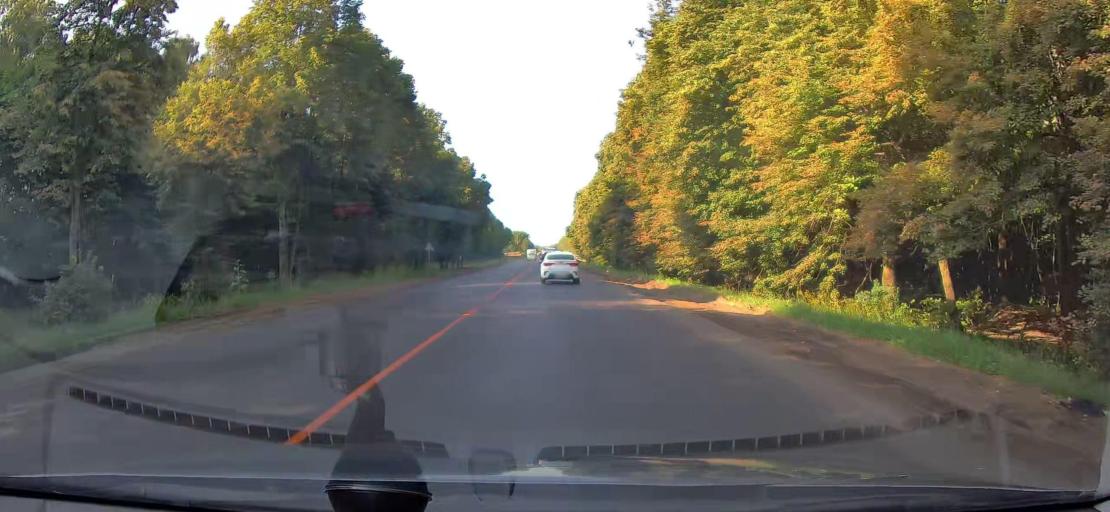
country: RU
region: Orjol
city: Spasskoye-Lutovinovo
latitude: 53.3594
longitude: 36.7226
